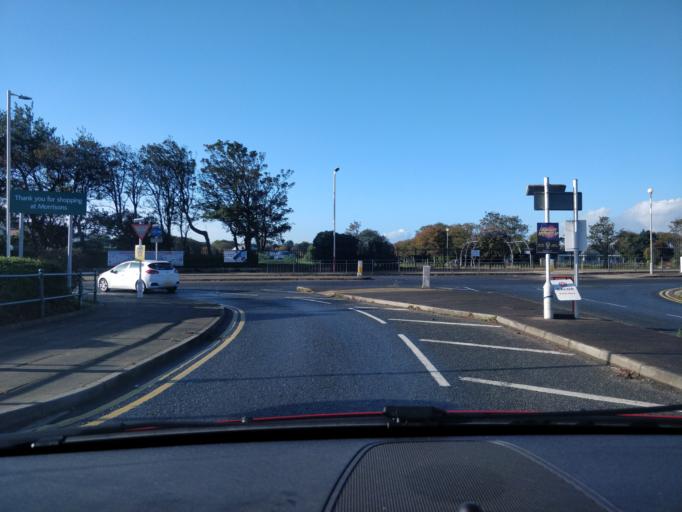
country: GB
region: England
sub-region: Sefton
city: Southport
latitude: 53.6461
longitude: -3.0157
